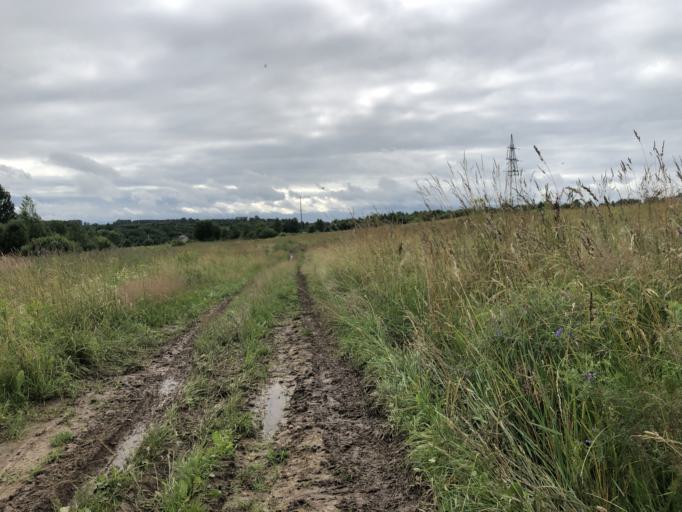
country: RU
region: Tverskaya
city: Rzhev
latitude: 56.2355
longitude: 34.3792
